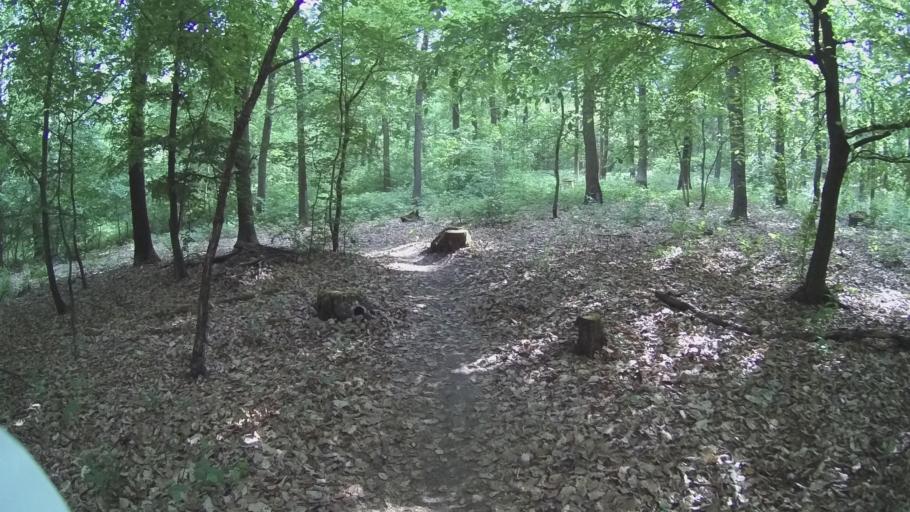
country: CZ
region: Central Bohemia
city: Zdiby
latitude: 50.2043
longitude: 14.4474
